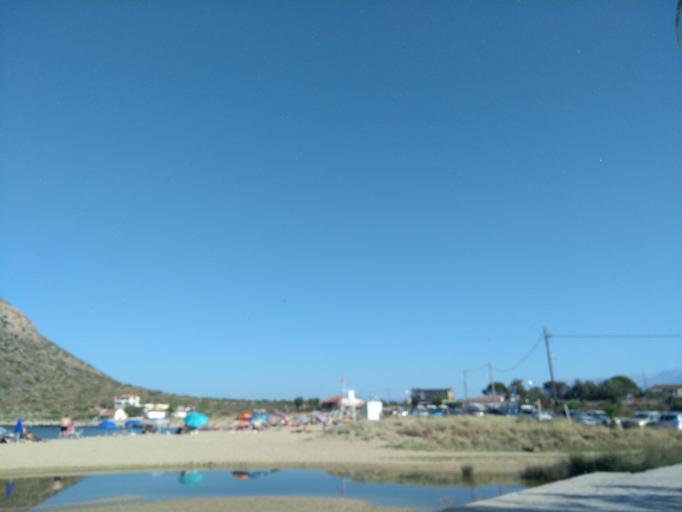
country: GR
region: Crete
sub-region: Nomos Chanias
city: Pithari
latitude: 35.5921
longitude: 24.0949
